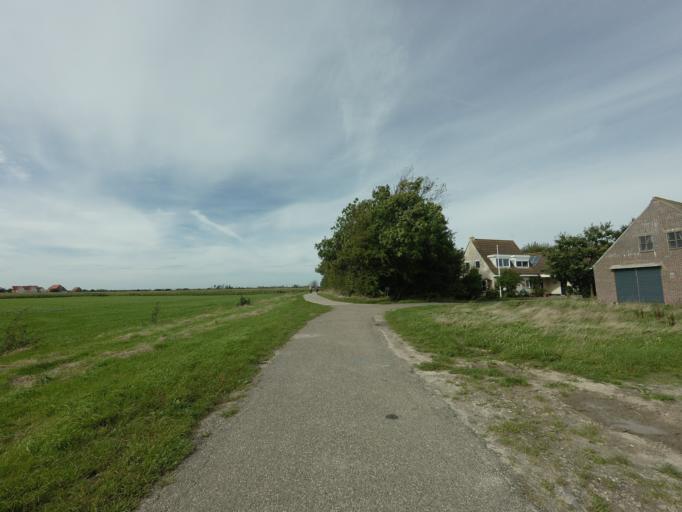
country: NL
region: North Holland
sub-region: Gemeente Texel
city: Den Burg
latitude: 53.0722
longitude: 4.8109
